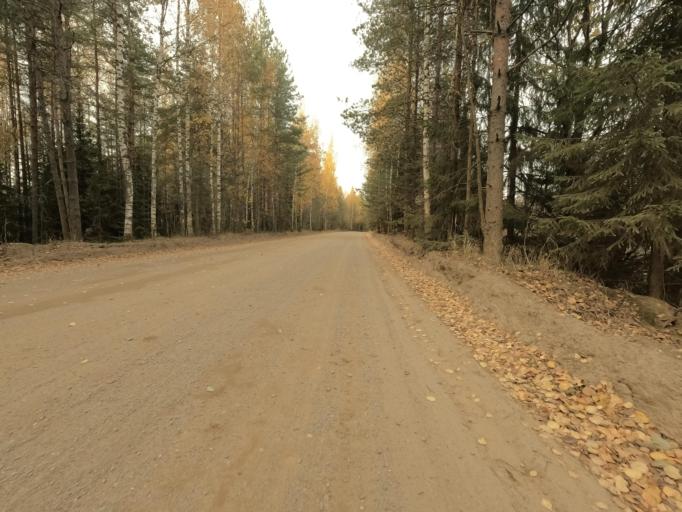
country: RU
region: Leningrad
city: Priladozhskiy
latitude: 59.6840
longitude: 31.3624
